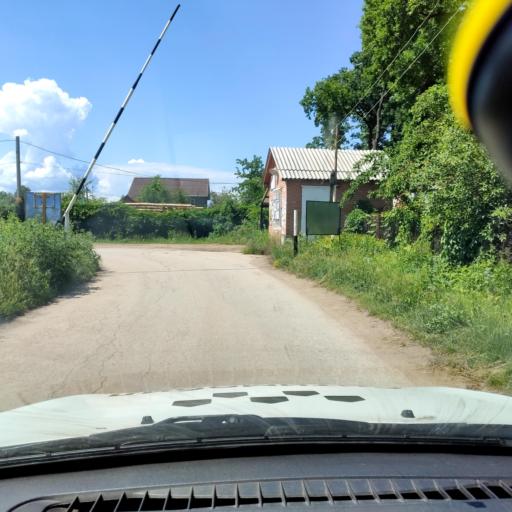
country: RU
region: Samara
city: Povolzhskiy
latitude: 53.4714
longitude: 49.6721
